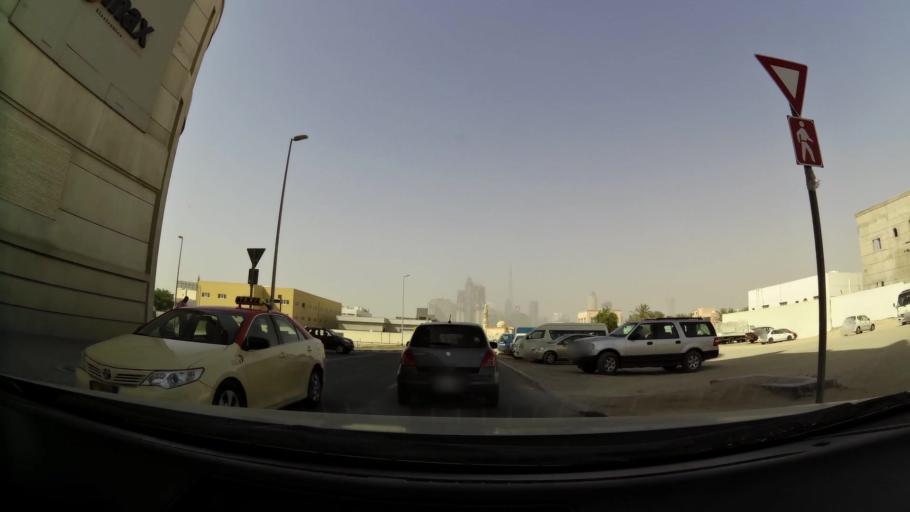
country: AE
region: Dubai
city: Dubai
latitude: 25.1696
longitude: 55.2427
